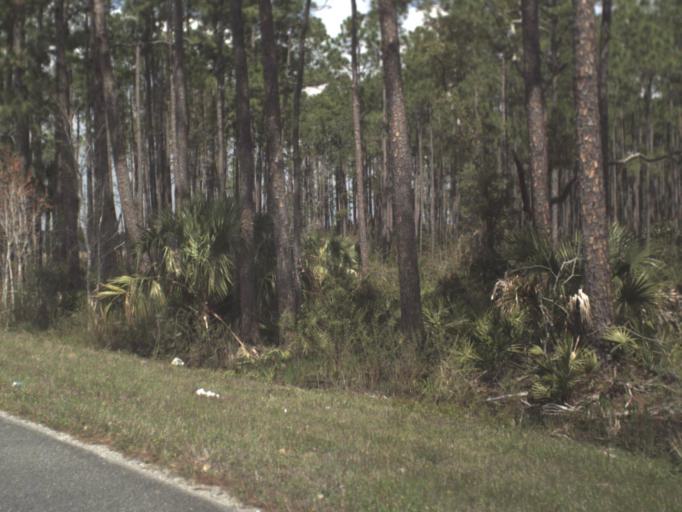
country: US
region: Florida
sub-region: Franklin County
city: Eastpoint
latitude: 29.8184
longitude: -84.8489
